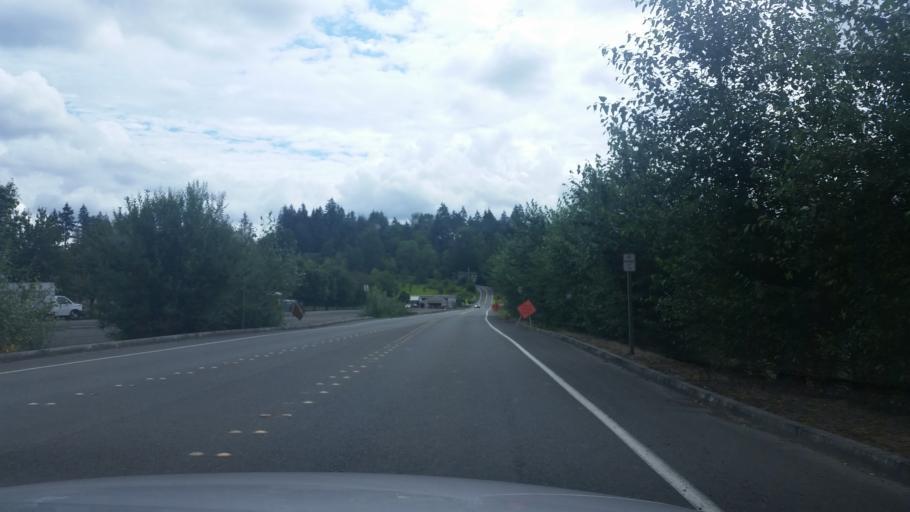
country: US
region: Washington
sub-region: King County
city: Redmond
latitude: 47.7040
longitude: -122.1411
